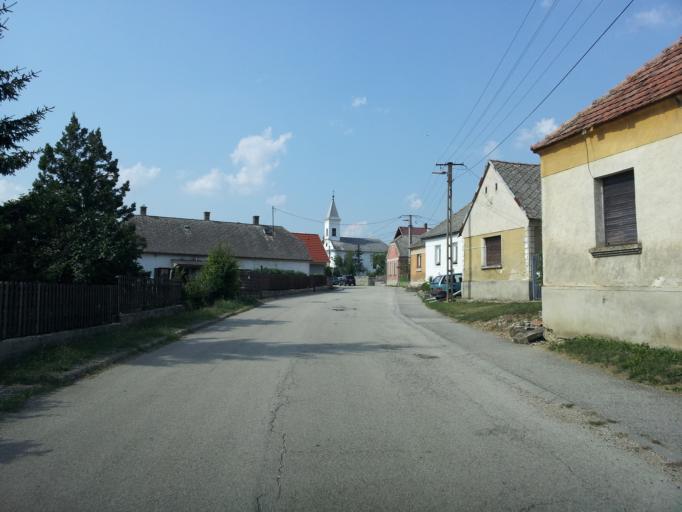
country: HU
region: Veszprem
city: Balatonfured
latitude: 47.0077
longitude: 17.7911
